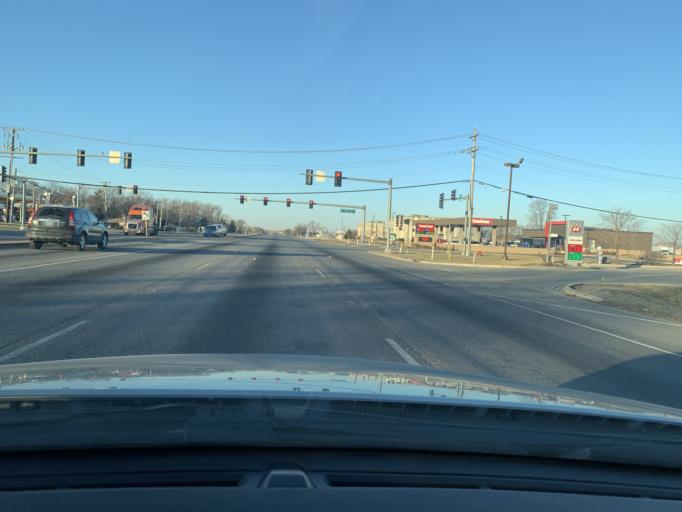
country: US
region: Illinois
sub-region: DuPage County
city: Wood Dale
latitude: 41.9713
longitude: -87.9591
